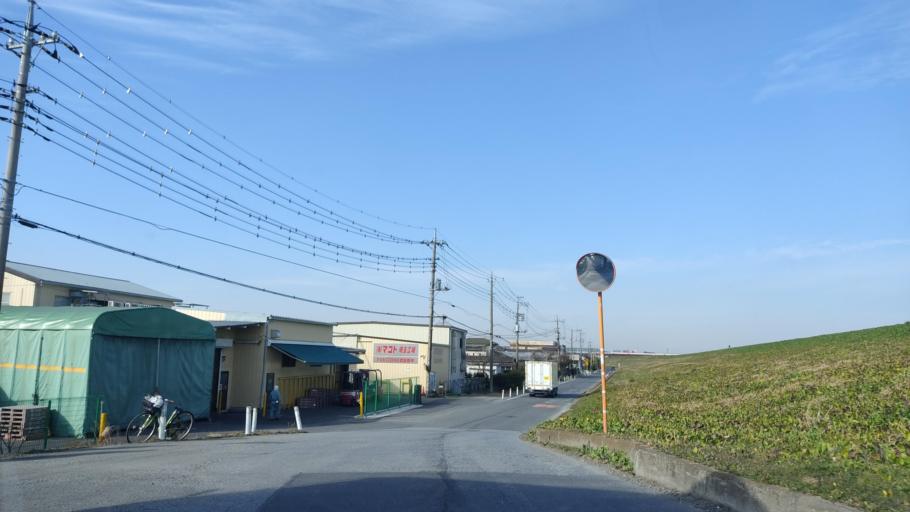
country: JP
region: Chiba
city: Nagareyama
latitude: 35.8673
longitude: 139.8949
